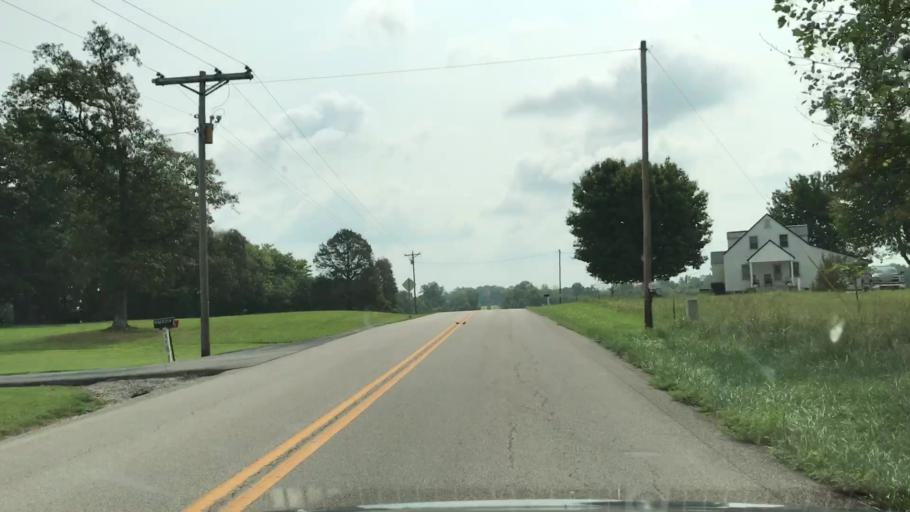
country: US
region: Kentucky
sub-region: Edmonson County
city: Brownsville
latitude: 37.1439
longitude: -86.1914
